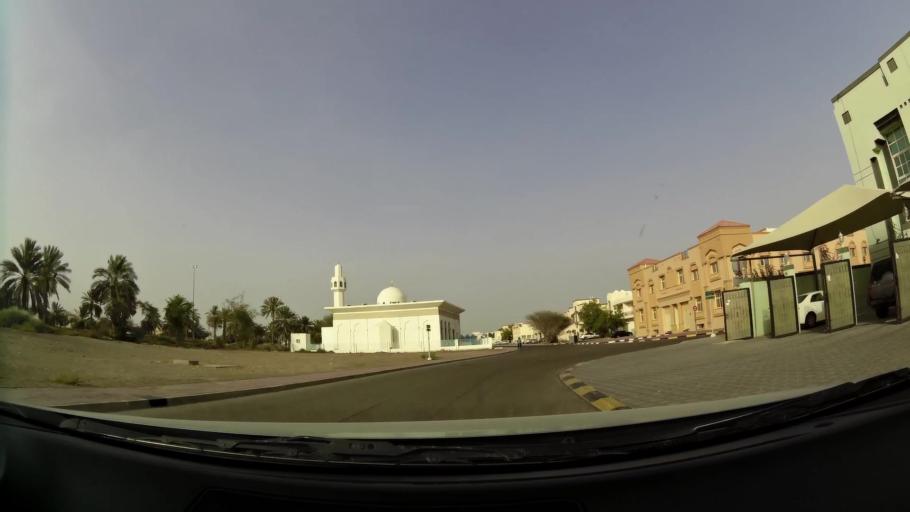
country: AE
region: Abu Dhabi
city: Al Ain
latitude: 24.2185
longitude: 55.6893
